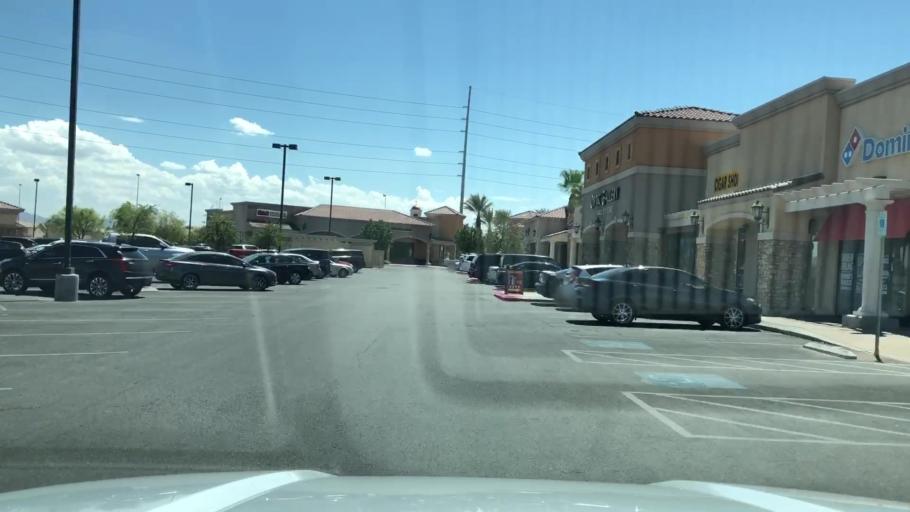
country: US
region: Nevada
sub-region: Clark County
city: Enterprise
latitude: 36.0345
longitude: -115.2073
